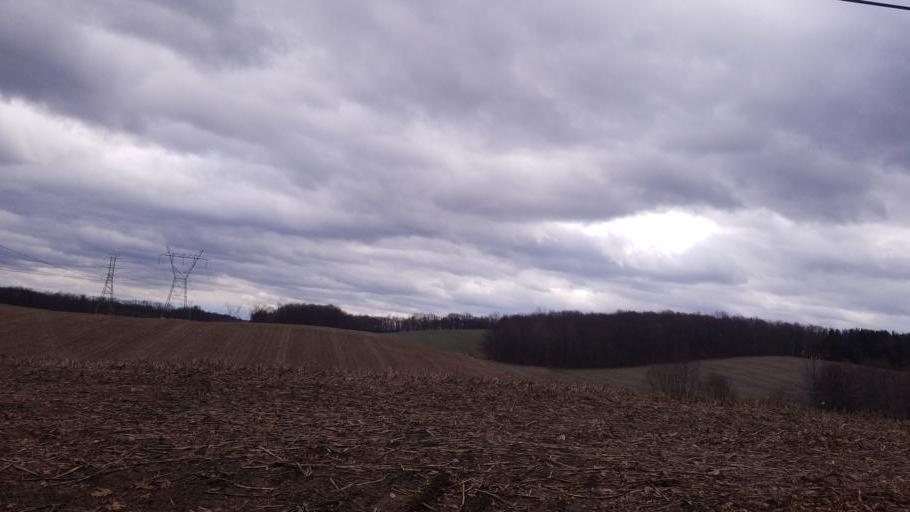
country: US
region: Ohio
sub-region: Licking County
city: Utica
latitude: 40.2092
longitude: -82.3909
